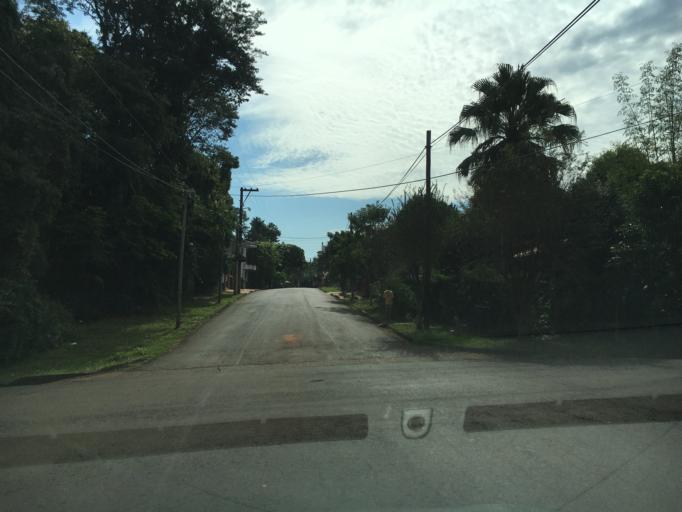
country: AR
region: Misiones
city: Puerto Rico
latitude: -26.8111
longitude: -55.0283
